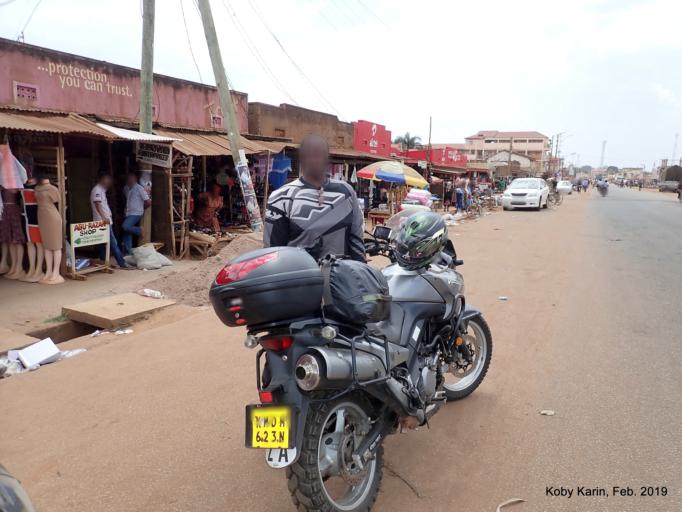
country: UG
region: Eastern Region
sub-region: Busia District
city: Busia
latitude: 0.4655
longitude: 34.0968
